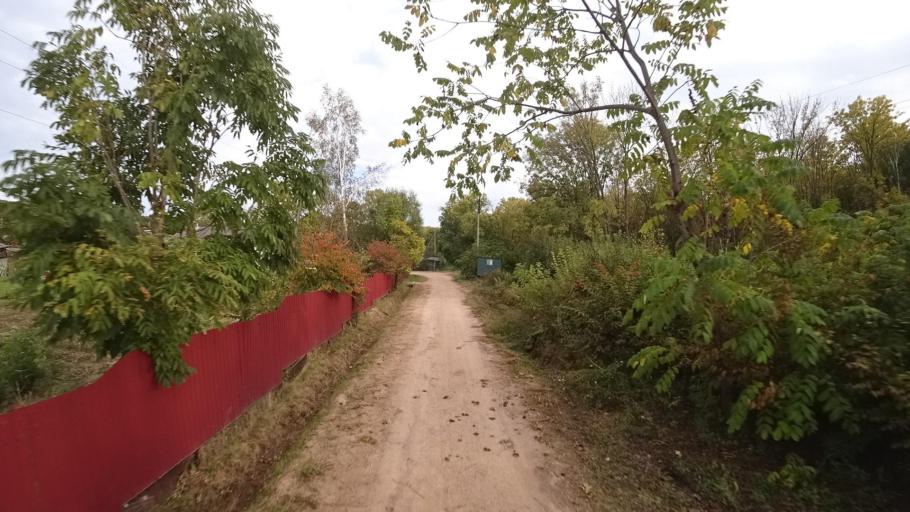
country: RU
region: Primorskiy
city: Yakovlevka
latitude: 44.4122
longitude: 133.4515
